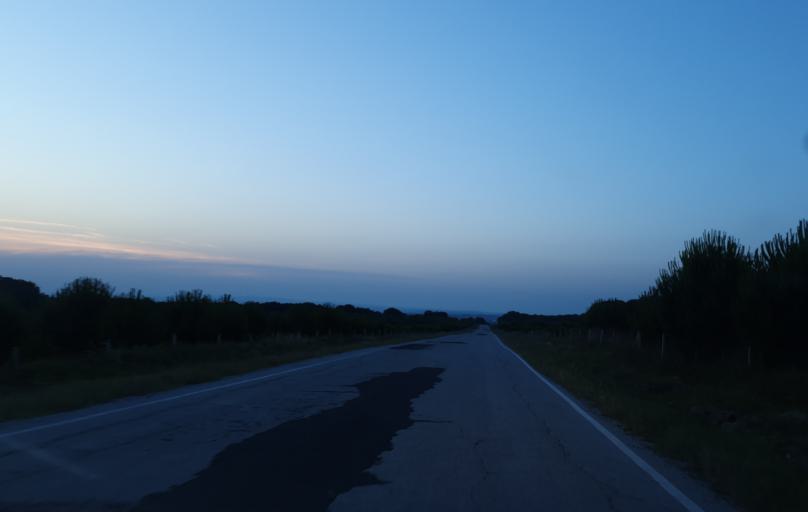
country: TR
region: Tekirdag
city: Cerkezkoey
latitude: 41.3491
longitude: 27.9285
